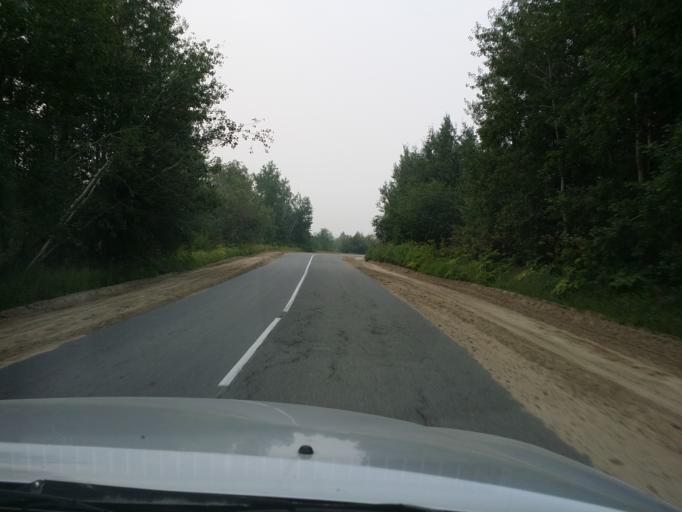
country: RU
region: Khanty-Mansiyskiy Avtonomnyy Okrug
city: Megion
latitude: 61.0141
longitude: 76.3139
